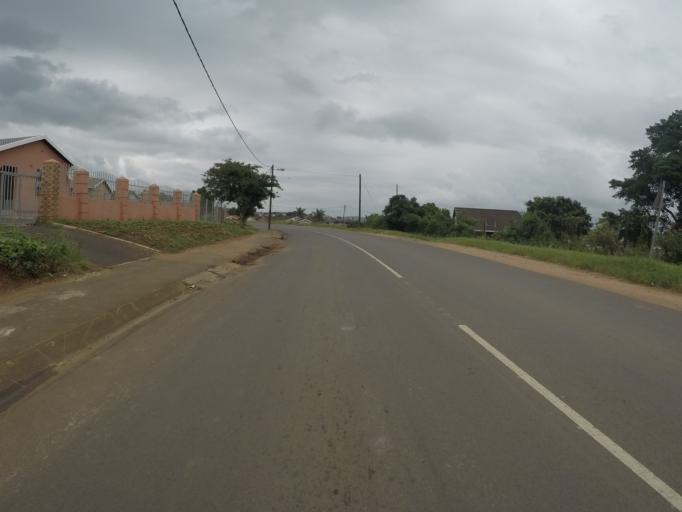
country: ZA
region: KwaZulu-Natal
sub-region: uThungulu District Municipality
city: Empangeni
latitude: -28.7830
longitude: 31.8556
